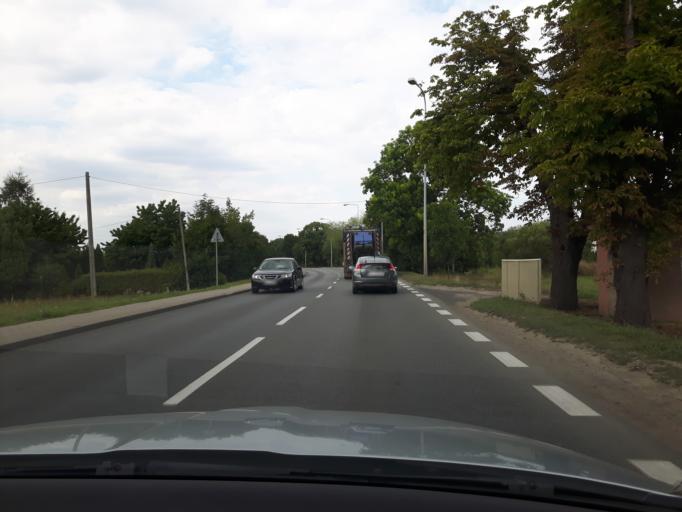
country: PL
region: Masovian Voivodeship
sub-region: Powiat legionowski
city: Stanislawow Pierwszy
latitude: 52.3573
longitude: 21.0289
